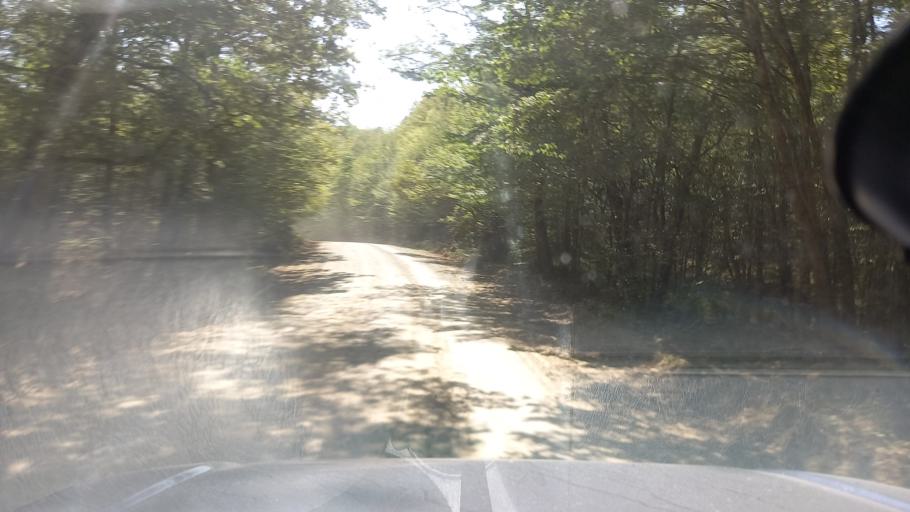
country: RU
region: Krasnodarskiy
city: Azovskaya
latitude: 44.6785
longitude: 38.6339
